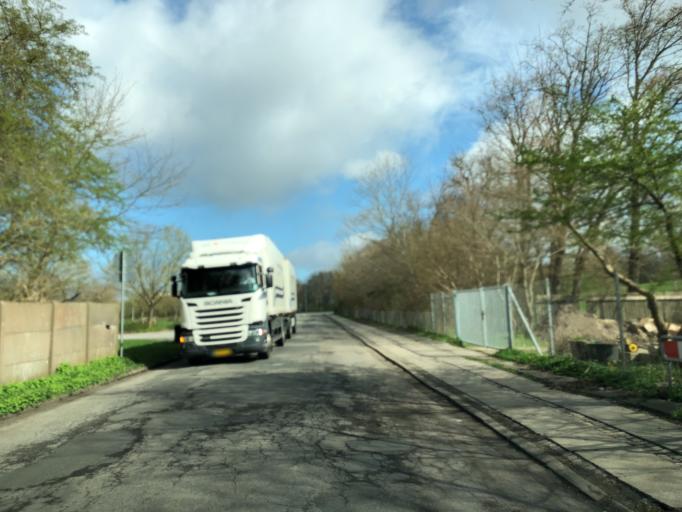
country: DK
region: North Denmark
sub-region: Alborg Kommune
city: Aalborg
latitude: 57.0533
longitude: 9.8837
